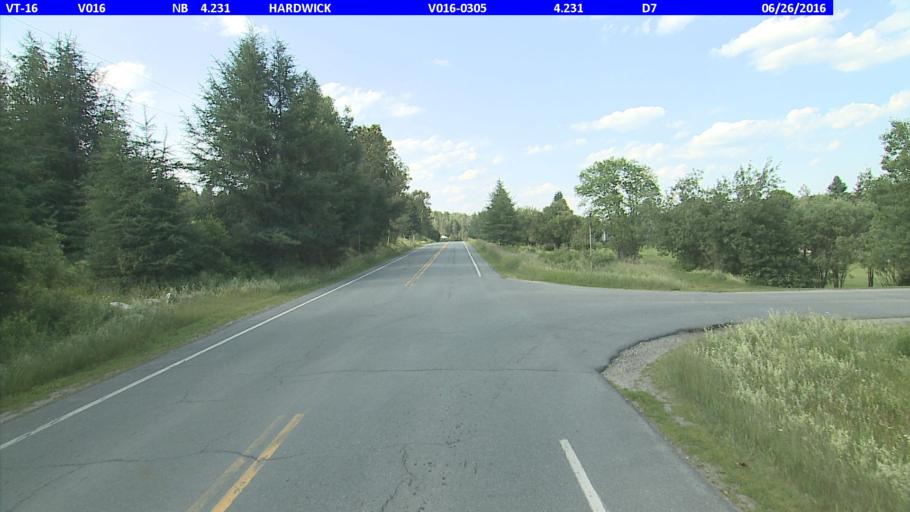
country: US
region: Vermont
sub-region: Caledonia County
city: Hardwick
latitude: 44.5420
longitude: -72.2695
